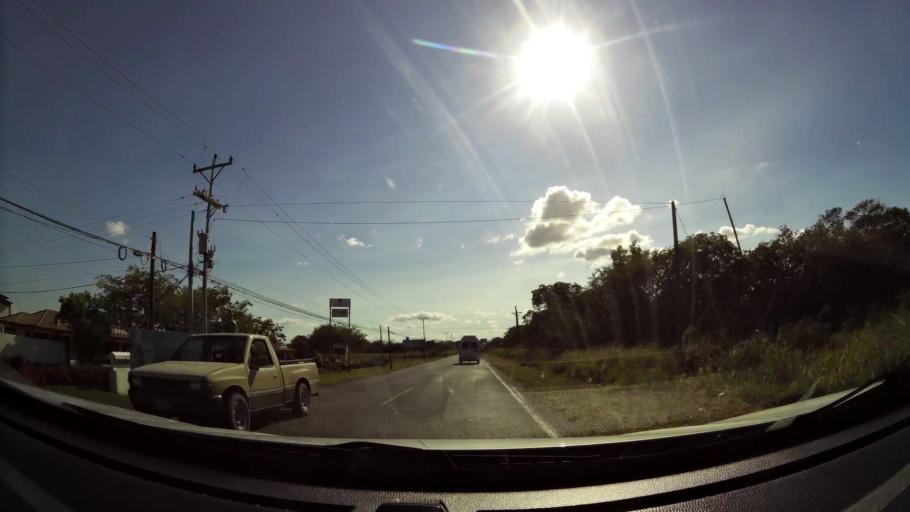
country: CR
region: Guanacaste
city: Sardinal
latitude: 10.5725
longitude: -85.5839
